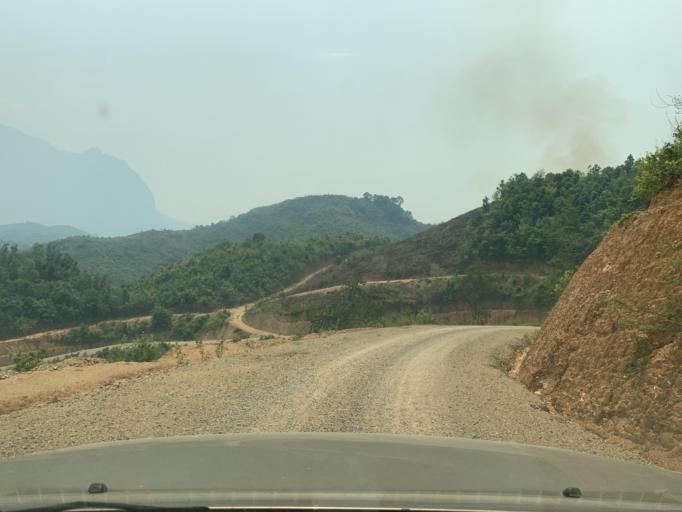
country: LA
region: Louangphabang
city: Louangphabang
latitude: 19.8613
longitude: 102.2570
